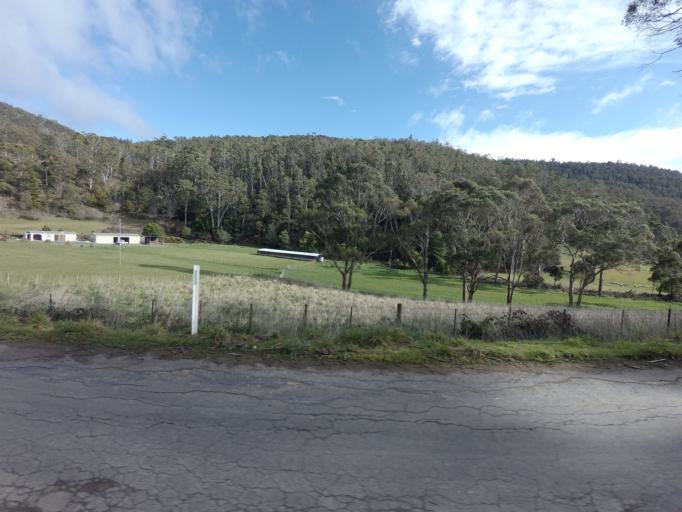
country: AU
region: Tasmania
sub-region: Derwent Valley
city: New Norfolk
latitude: -42.7895
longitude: 146.9462
